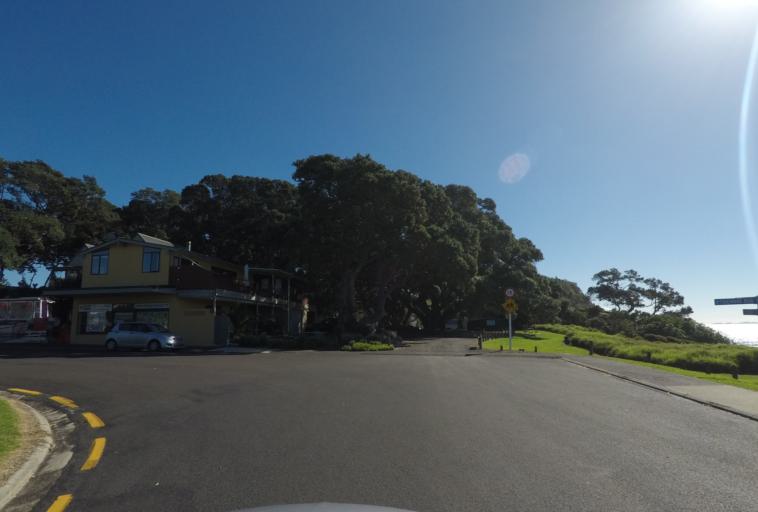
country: NZ
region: Waikato
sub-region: Thames-Coromandel District
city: Whangamata
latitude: -37.2802
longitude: 175.9008
